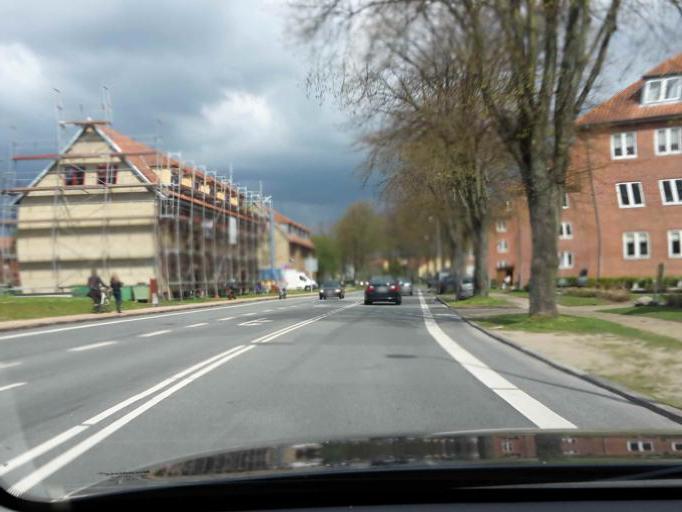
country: DK
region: South Denmark
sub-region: Odense Kommune
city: Odense
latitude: 55.3904
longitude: 10.3497
